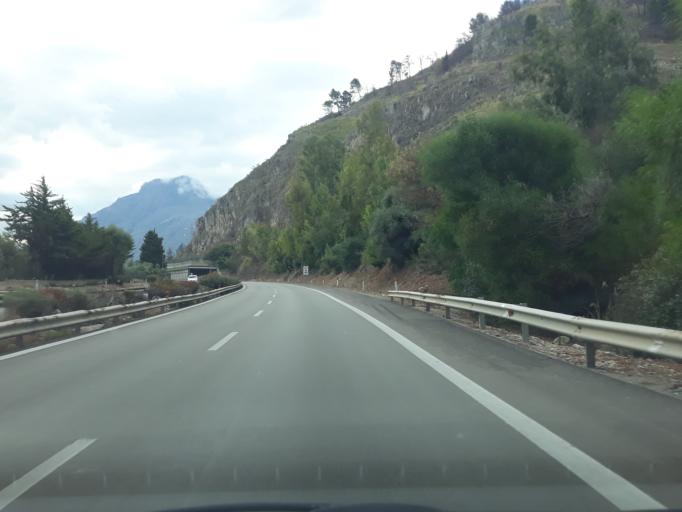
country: IT
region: Sicily
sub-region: Palermo
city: Trabia
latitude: 37.9851
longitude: 13.6577
